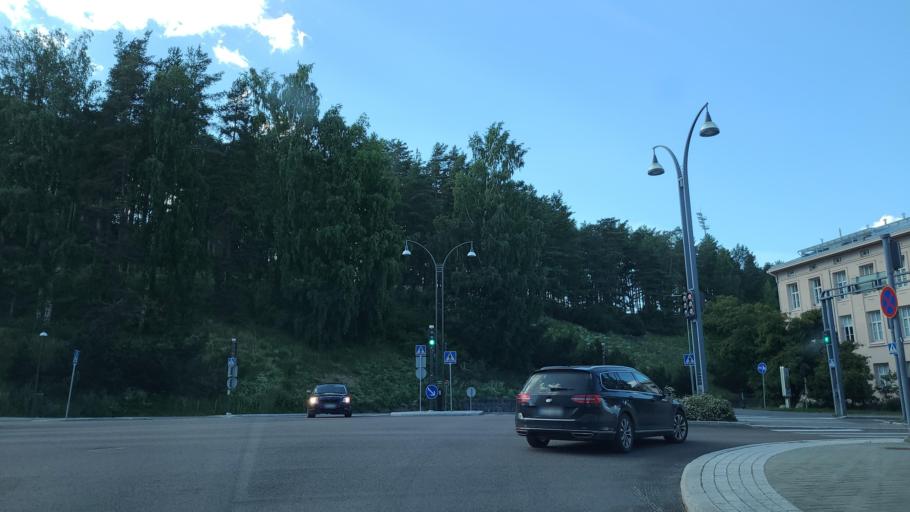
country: FI
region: Central Finland
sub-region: Jyvaeskylae
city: Jyvaeskylae
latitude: 62.2424
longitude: 25.7432
